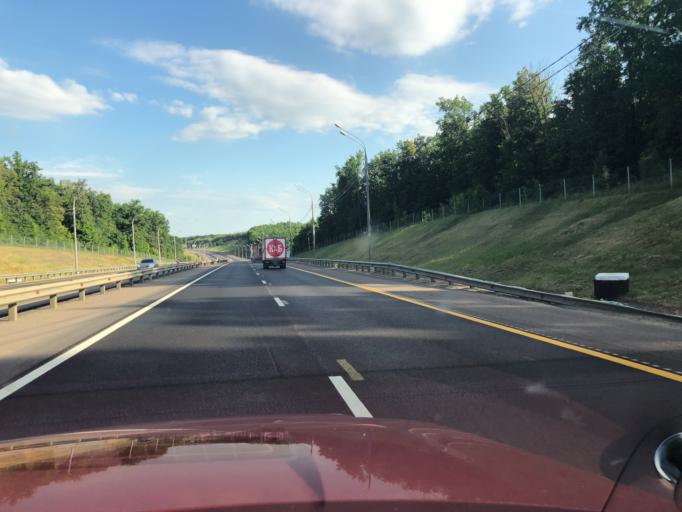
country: RU
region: Lipetsk
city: Zadonsk
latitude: 52.3964
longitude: 38.8611
